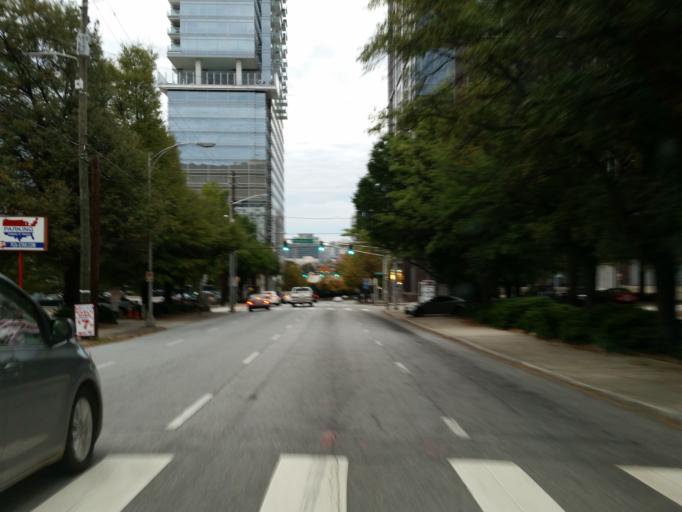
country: US
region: Georgia
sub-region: Fulton County
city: Atlanta
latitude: 33.7634
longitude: -84.3890
